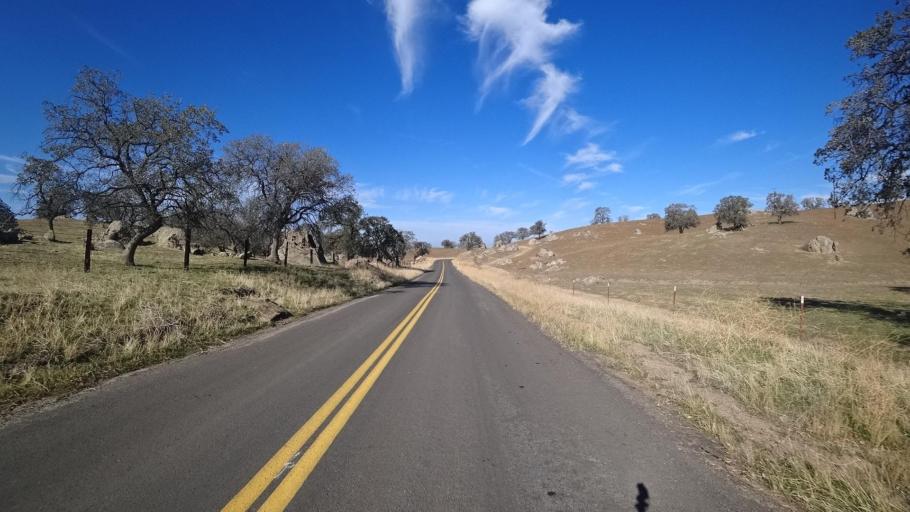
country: US
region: California
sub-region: Kern County
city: Oildale
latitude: 35.6211
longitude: -118.8488
